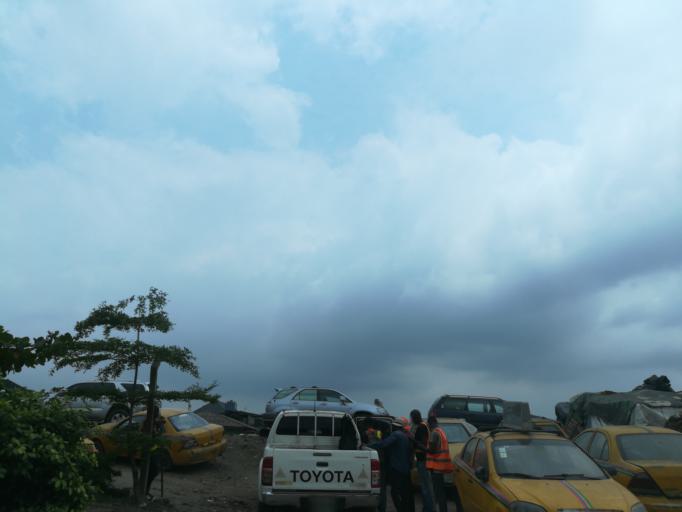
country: NG
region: Lagos
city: Agege
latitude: 6.6185
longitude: 3.3262
